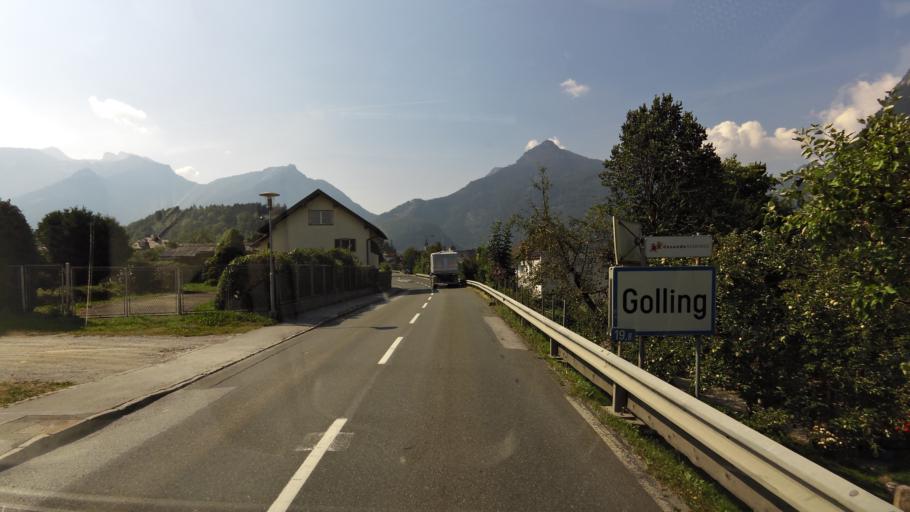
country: AT
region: Salzburg
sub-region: Politischer Bezirk Hallein
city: Golling an der Salzach
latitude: 47.6028
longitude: 13.1681
